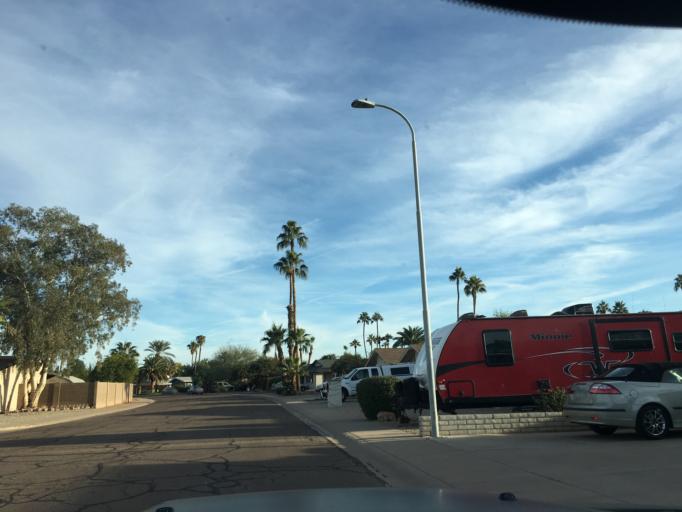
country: US
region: Arizona
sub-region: Maricopa County
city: Tempe
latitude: 33.3698
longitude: -111.9046
